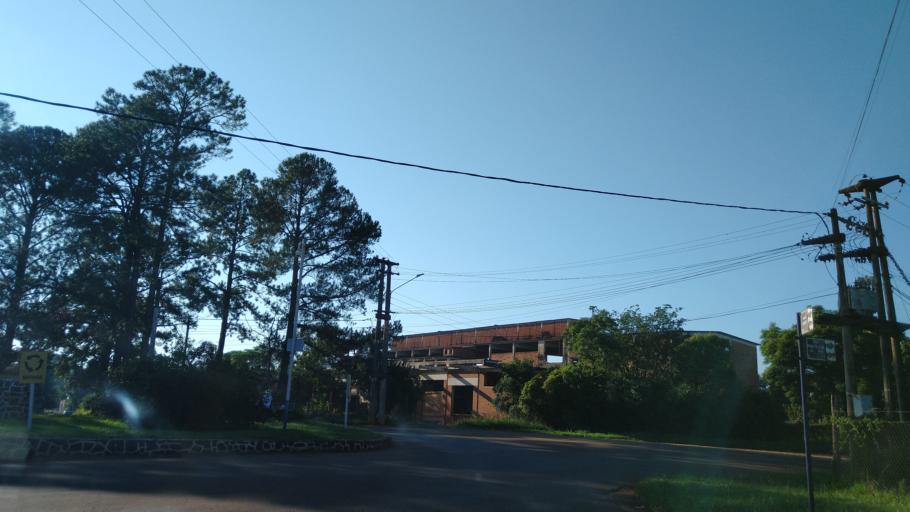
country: AR
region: Misiones
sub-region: Departamento de Montecarlo
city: Montecarlo
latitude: -26.5751
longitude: -54.7457
